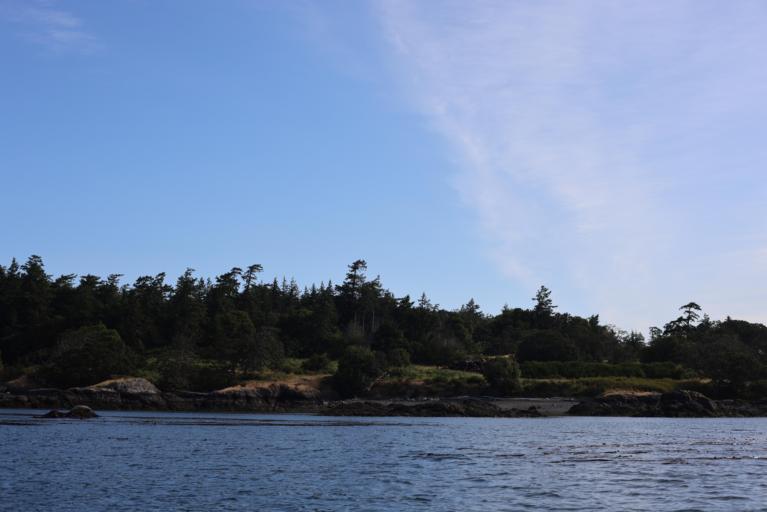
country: CA
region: British Columbia
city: Metchosin
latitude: 48.3375
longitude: -123.5463
